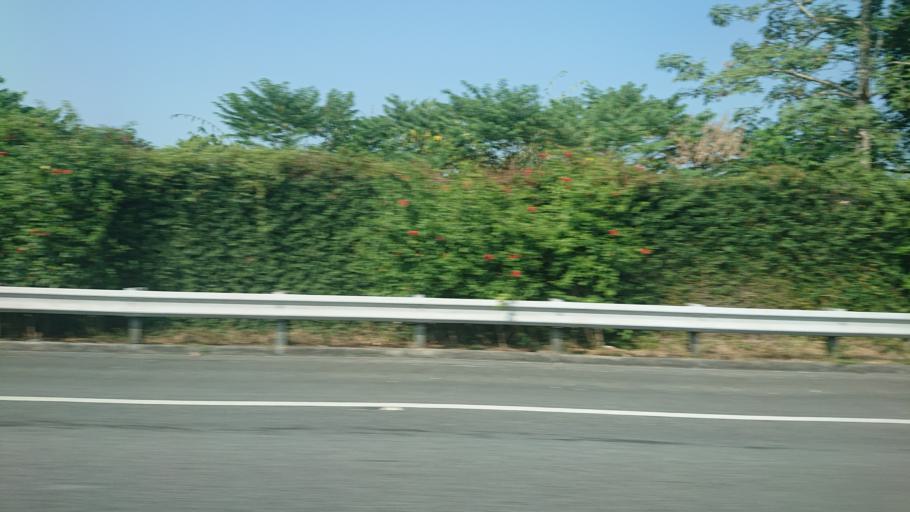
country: TW
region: Taiwan
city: Lugu
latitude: 23.7840
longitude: 120.7038
